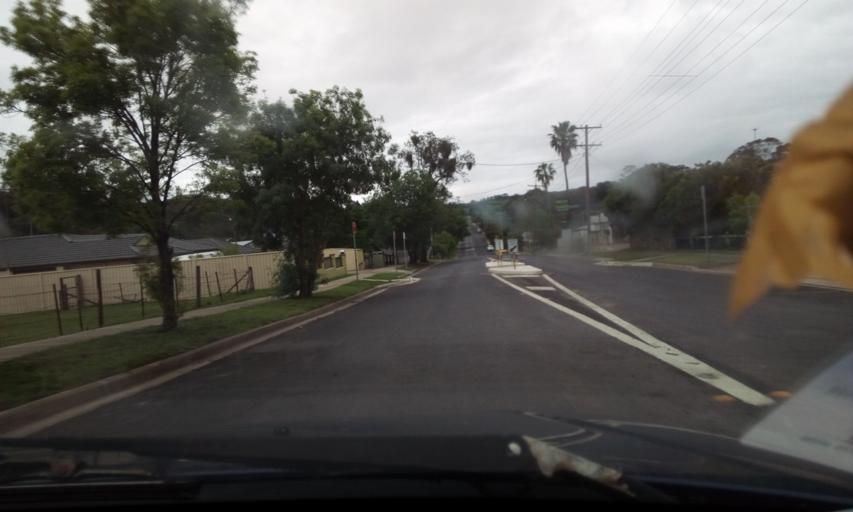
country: AU
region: New South Wales
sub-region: Wollondilly
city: Douglas Park
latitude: -34.1829
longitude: 150.7107
